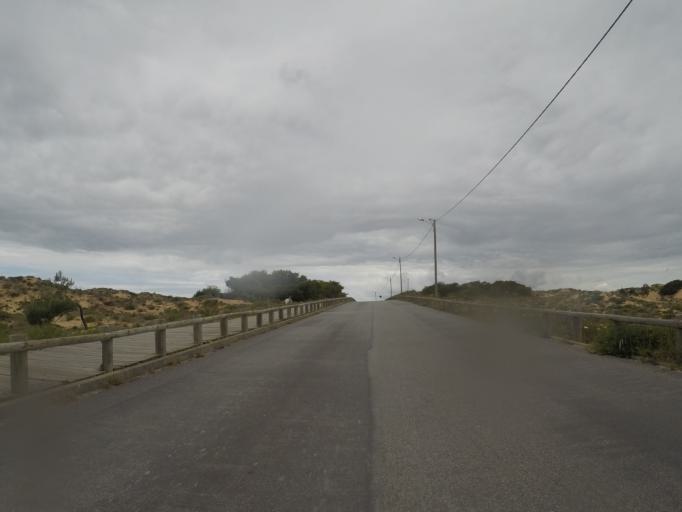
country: PT
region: Beja
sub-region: Odemira
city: Vila Nova de Milfontes
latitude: 37.6526
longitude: -8.7965
